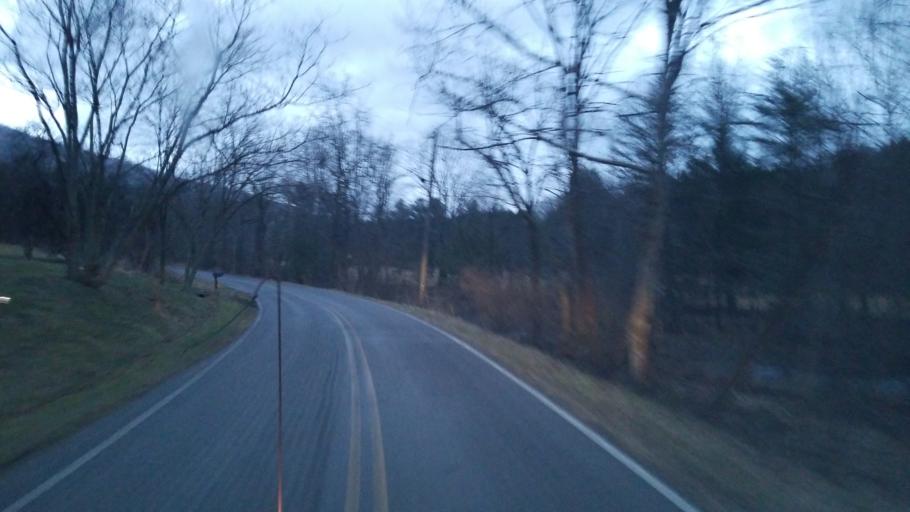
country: US
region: Virginia
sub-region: Pulaski County
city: Pulaski
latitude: 37.1280
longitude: -80.8615
